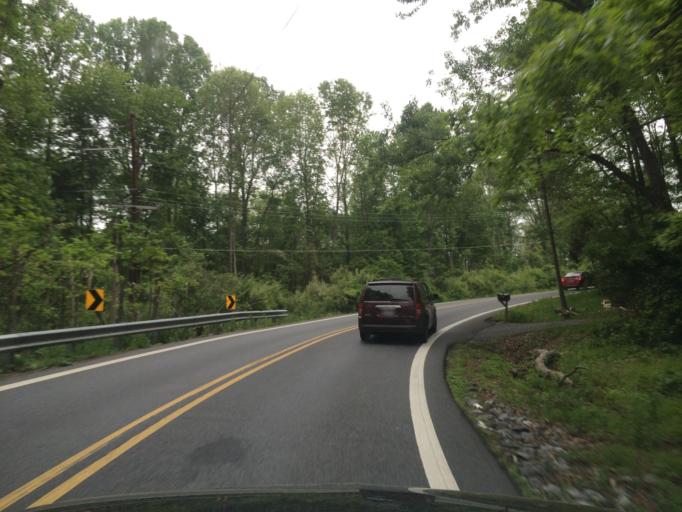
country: US
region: Maryland
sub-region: Carroll County
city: Eldersburg
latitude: 39.3769
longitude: -76.9111
